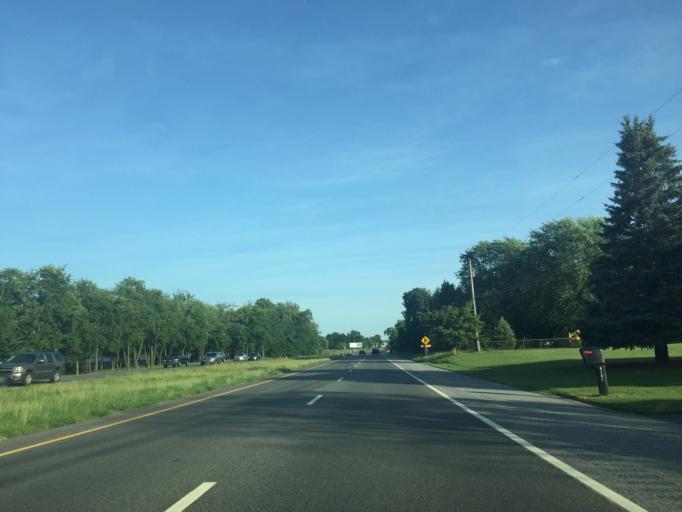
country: US
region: Delaware
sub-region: Kent County
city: Cheswold
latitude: 39.2330
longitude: -75.5815
